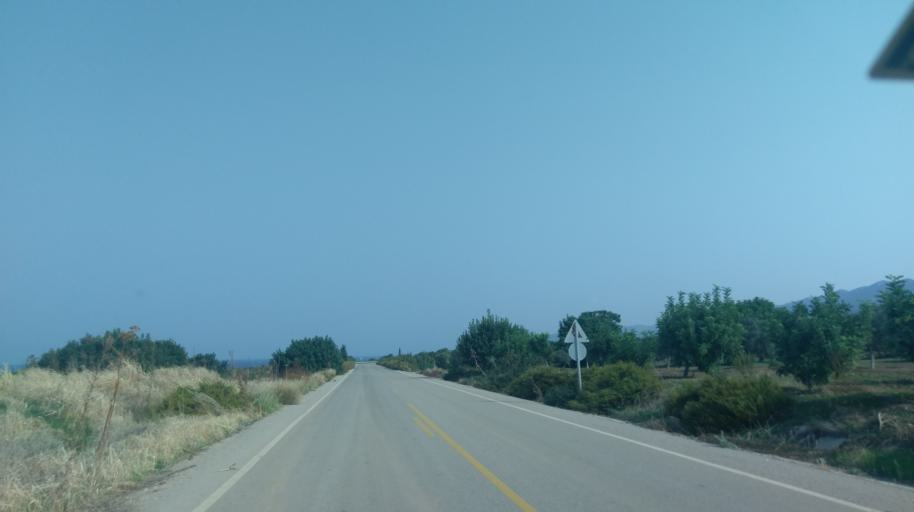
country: CY
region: Ammochostos
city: Trikomo
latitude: 35.4402
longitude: 33.9522
